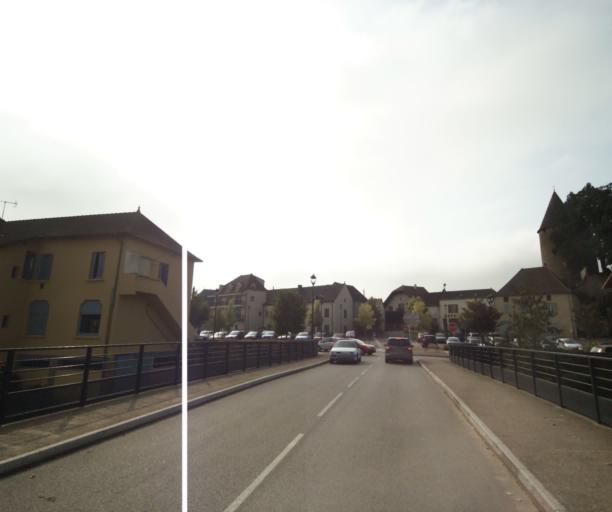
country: FR
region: Bourgogne
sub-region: Departement de Saone-et-Loire
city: Charolles
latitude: 46.4366
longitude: 4.2778
